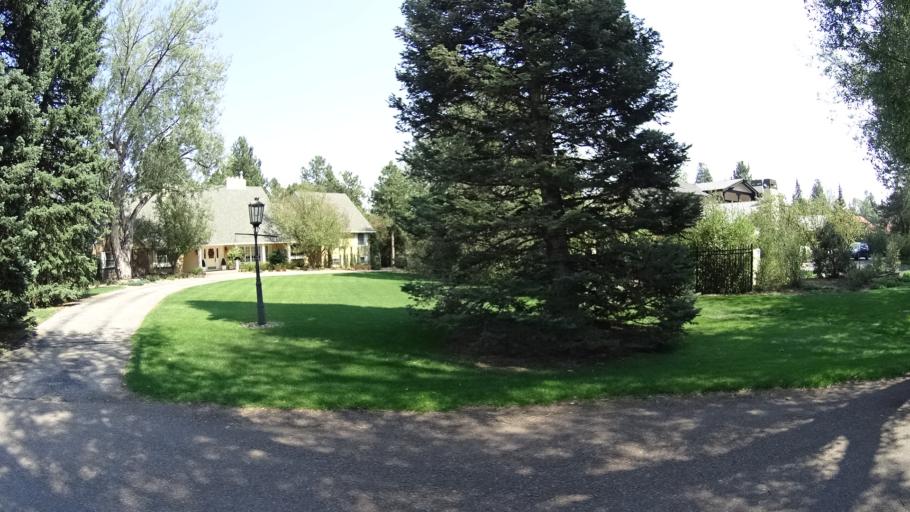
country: US
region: Colorado
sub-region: El Paso County
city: Colorado Springs
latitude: 38.7950
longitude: -104.8416
